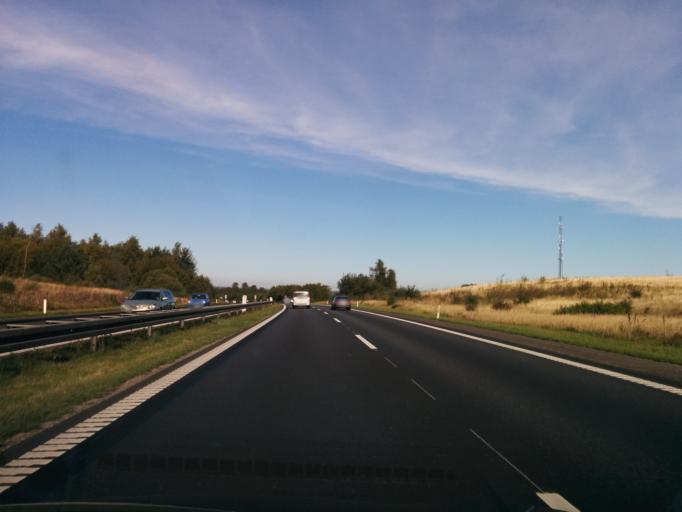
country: DK
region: Central Jutland
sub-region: Skanderborg Kommune
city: Skanderborg
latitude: 55.9762
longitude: 9.8671
